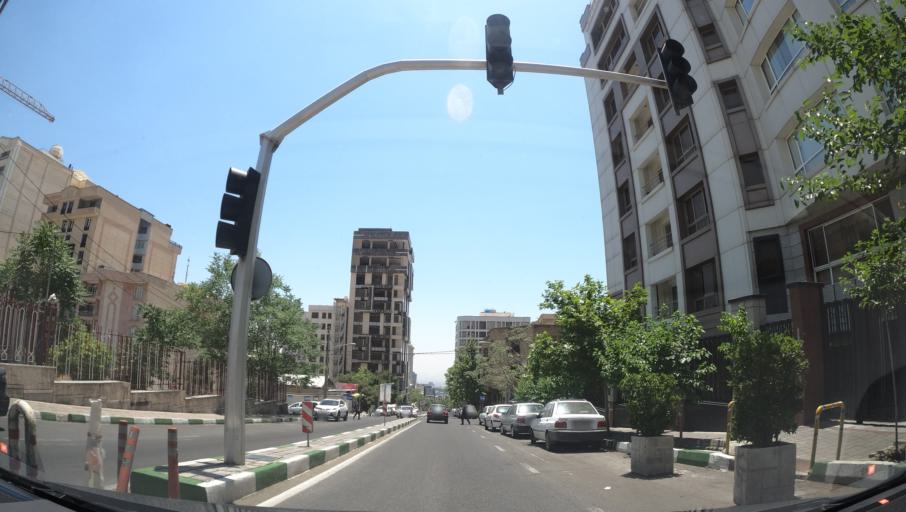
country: IR
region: Tehran
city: Tajrish
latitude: 35.8077
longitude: 51.4012
